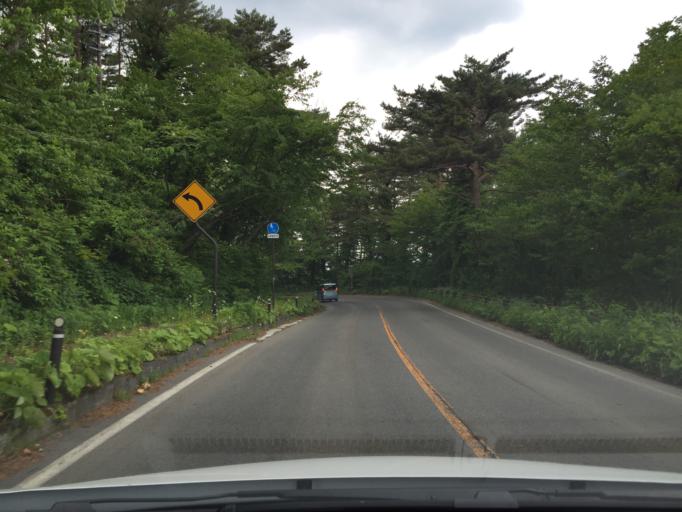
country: JP
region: Fukushima
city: Inawashiro
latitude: 37.6559
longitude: 140.0674
